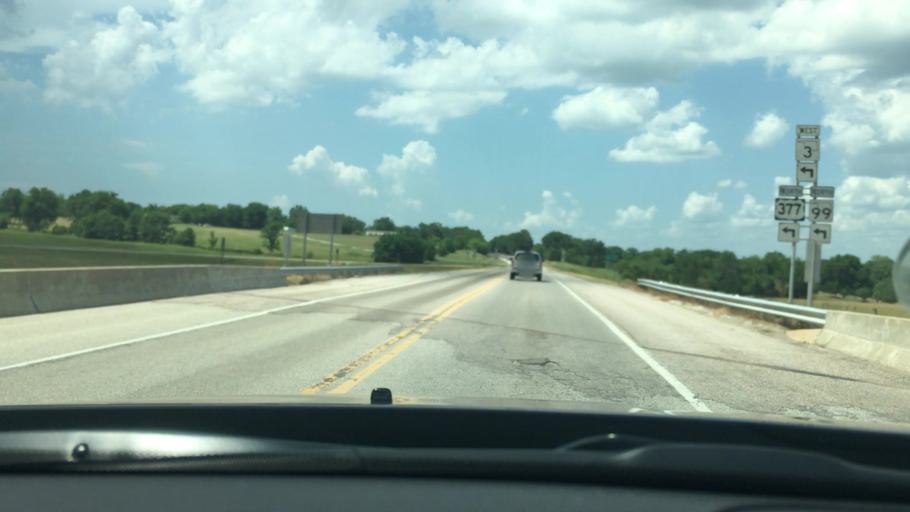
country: US
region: Oklahoma
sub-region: Pontotoc County
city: Ada
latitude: 34.7266
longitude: -96.6348
